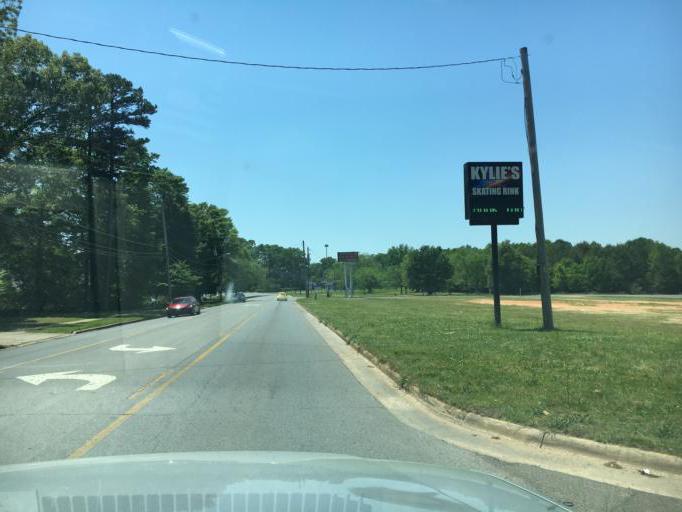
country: US
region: North Carolina
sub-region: Cleveland County
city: Shelby
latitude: 35.2720
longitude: -81.5492
